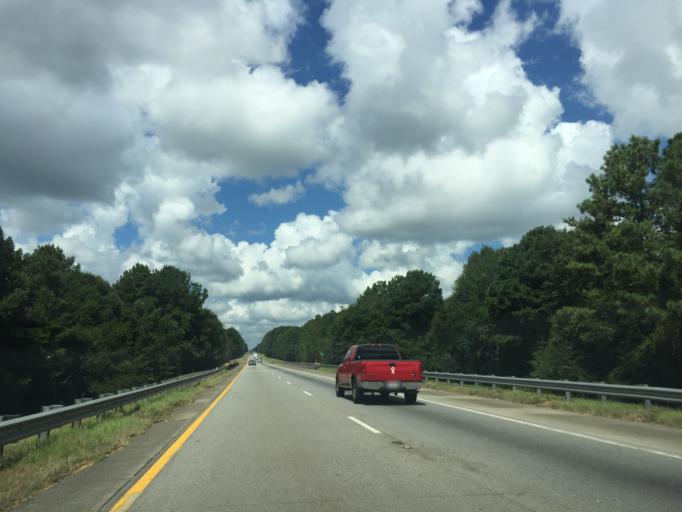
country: US
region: Georgia
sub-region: Candler County
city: Metter
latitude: 32.3844
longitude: -82.2408
